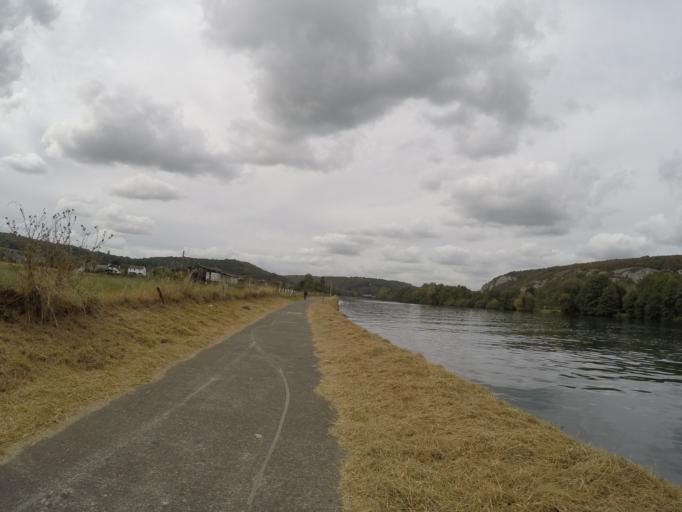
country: BE
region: Wallonia
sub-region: Province de Namur
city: Anhee
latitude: 50.3060
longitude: 4.8904
